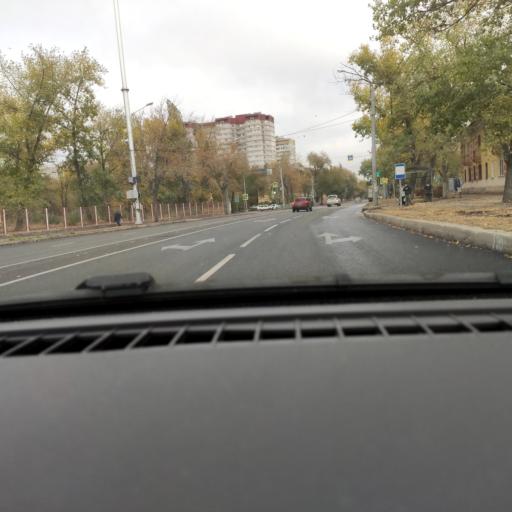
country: RU
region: Voronezj
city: Maslovka
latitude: 51.6141
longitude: 39.2470
